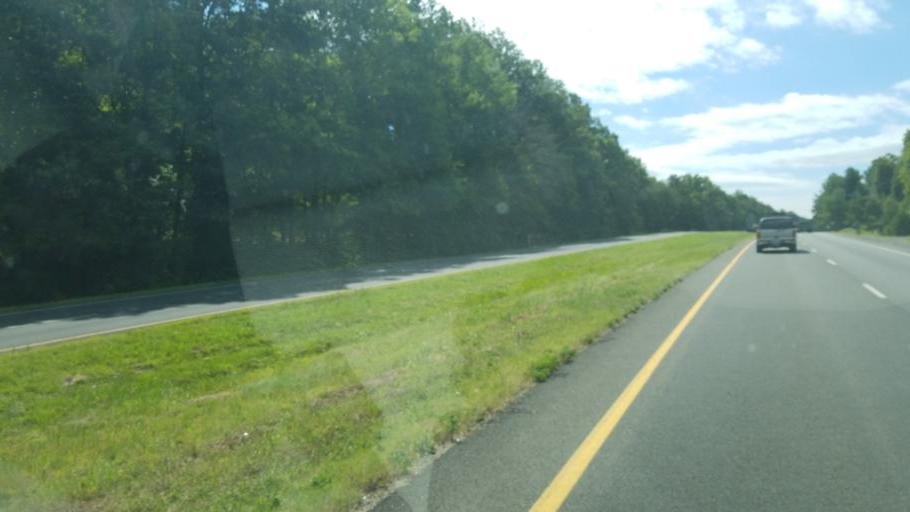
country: US
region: Virginia
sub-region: Fauquier County
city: Bealeton
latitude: 38.4959
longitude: -77.6878
